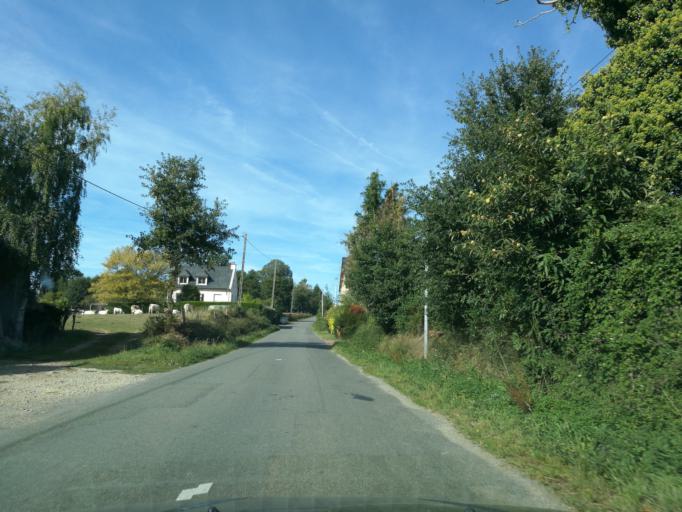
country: FR
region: Brittany
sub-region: Departement d'Ille-et-Vilaine
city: Breteil
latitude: 48.1604
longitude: -1.8956
